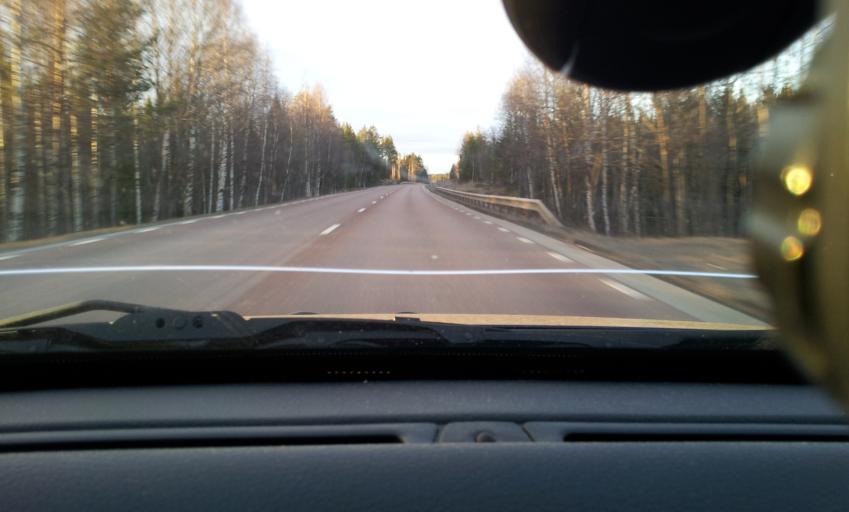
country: SE
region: Jaemtland
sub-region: Bergs Kommun
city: Hoverberg
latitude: 62.8805
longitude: 14.5224
